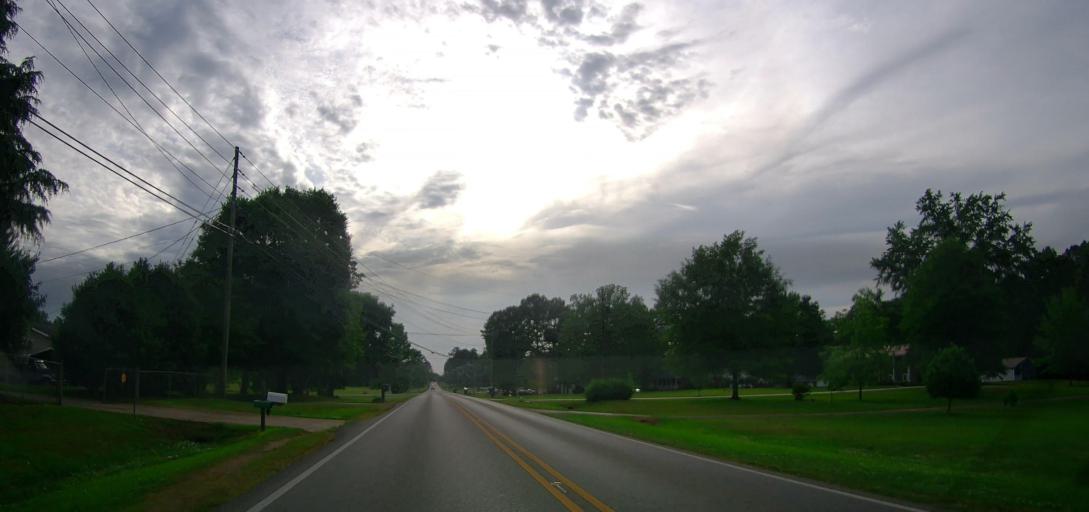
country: US
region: Alabama
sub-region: Calhoun County
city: Oxford
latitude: 33.5855
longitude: -85.7892
